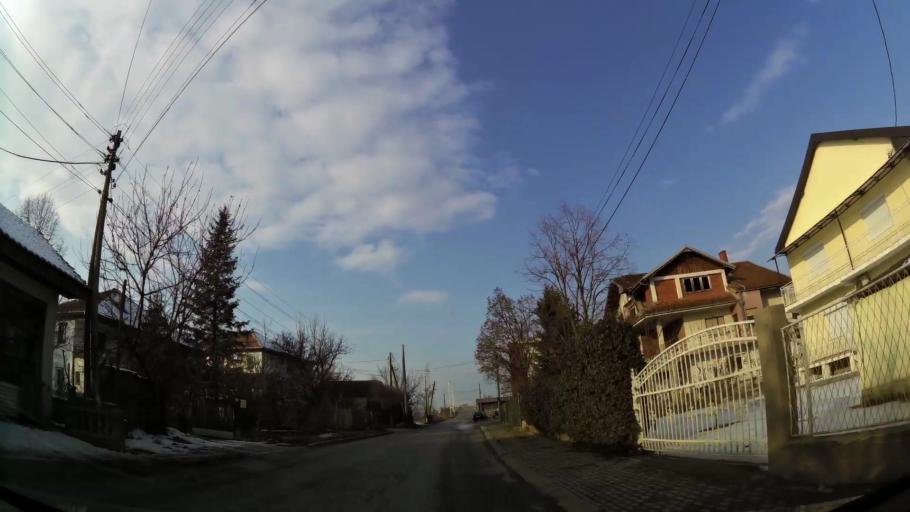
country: MK
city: Creshevo
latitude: 42.0291
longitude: 21.5125
